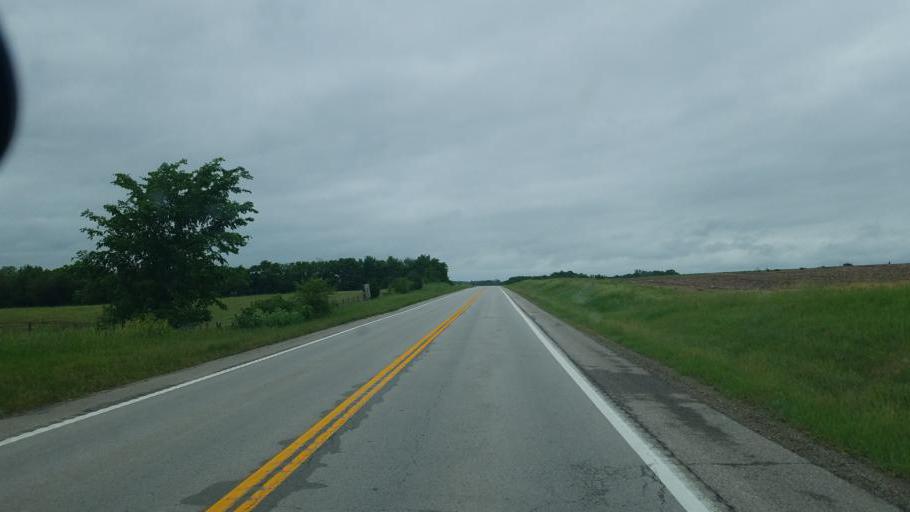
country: US
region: Missouri
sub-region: Carroll County
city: Carrollton
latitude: 39.5050
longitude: -93.4755
